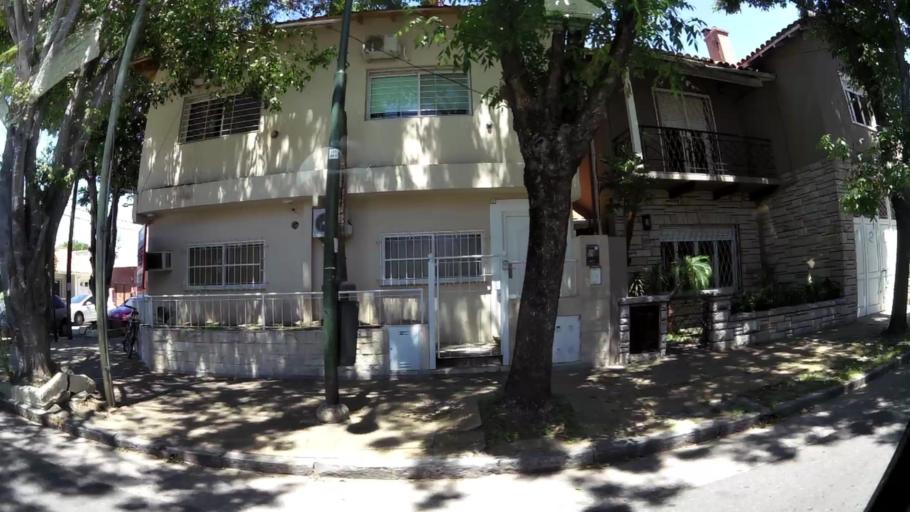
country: AR
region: Buenos Aires
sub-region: Partido de San Isidro
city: San Isidro
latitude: -34.4934
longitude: -58.5087
